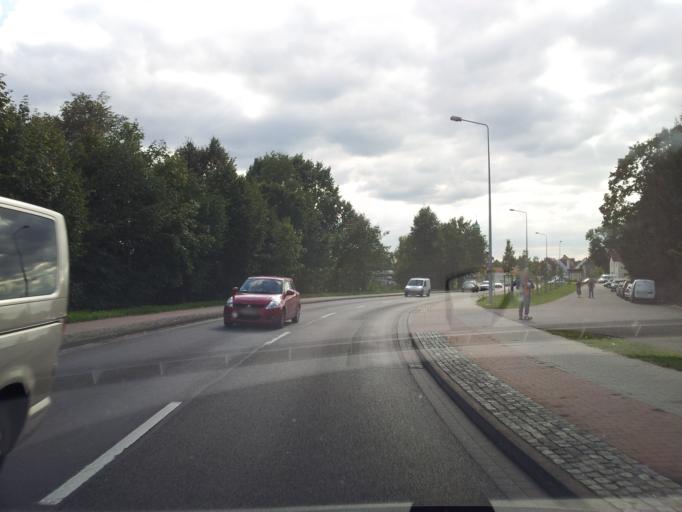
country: DE
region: Brandenburg
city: Ruhland
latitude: 51.4627
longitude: 13.8698
